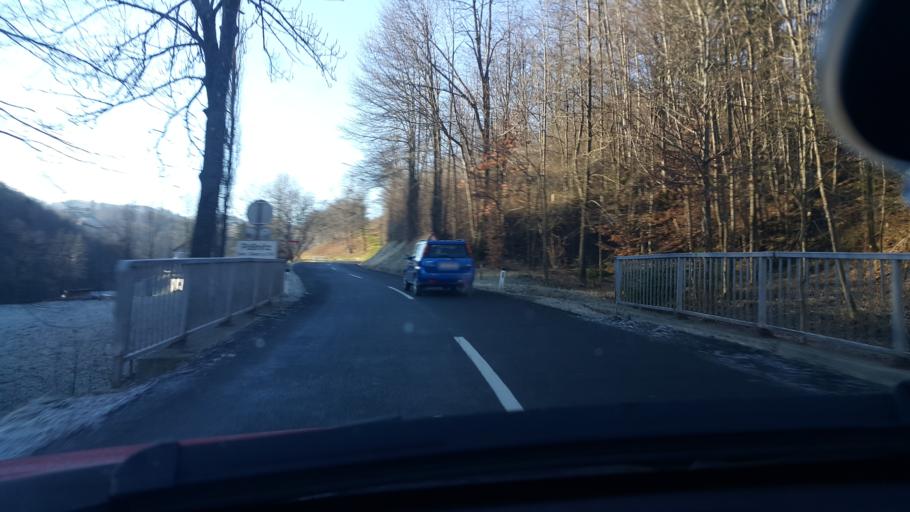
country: AT
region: Styria
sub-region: Politischer Bezirk Leibnitz
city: Sulztal an der Weinstrasse
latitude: 46.6500
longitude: 15.5291
